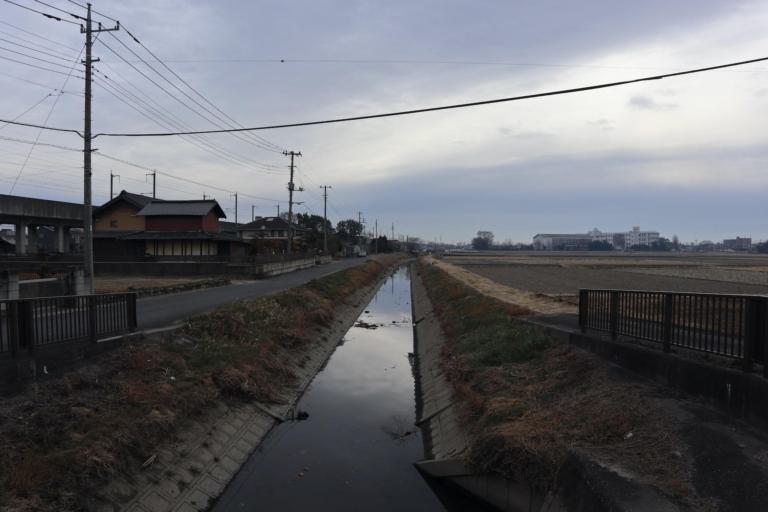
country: JP
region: Saitama
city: Fukiage-fujimi
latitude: 36.1161
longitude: 139.4504
